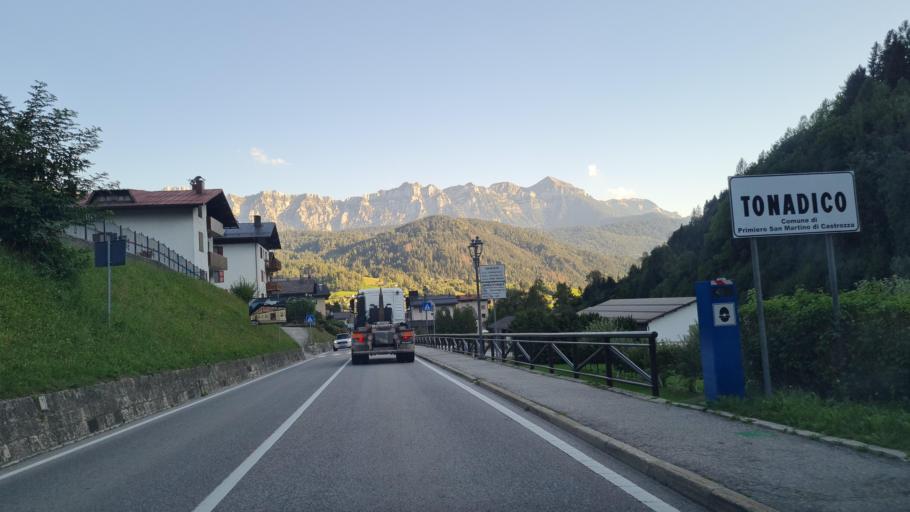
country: IT
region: Trentino-Alto Adige
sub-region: Provincia di Trento
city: Siror
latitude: 46.1858
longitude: 11.8308
